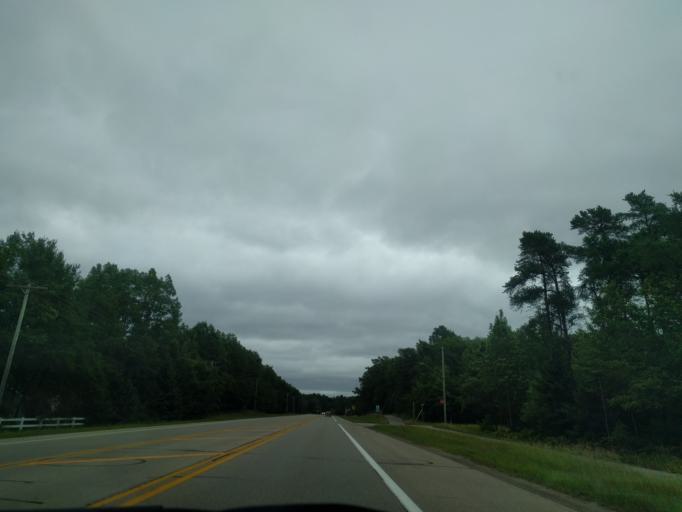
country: US
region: Michigan
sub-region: Delta County
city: Gladstone
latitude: 45.8556
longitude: -87.0438
